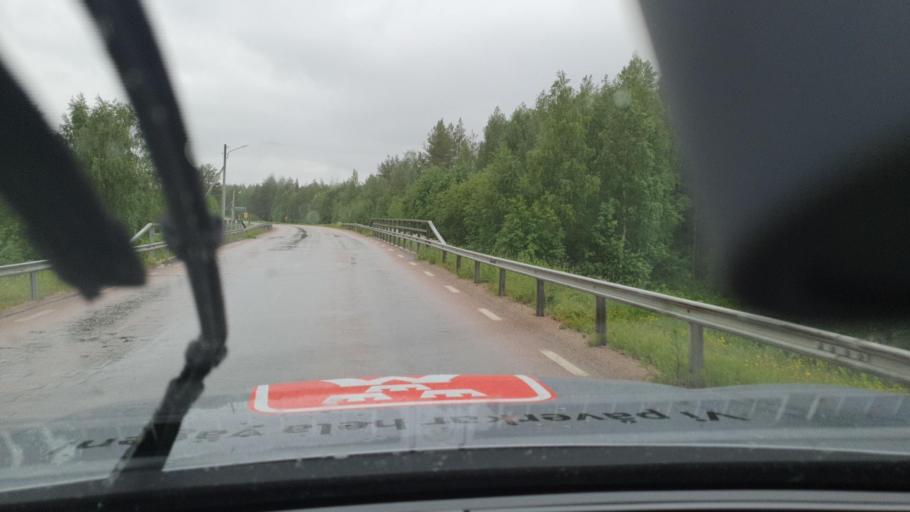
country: SE
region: Norrbotten
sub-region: Overkalix Kommun
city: OEverkalix
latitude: 66.3858
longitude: 22.9267
